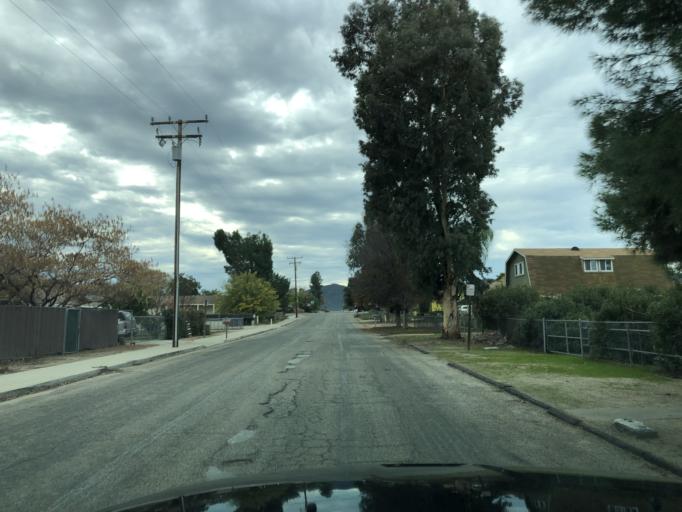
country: US
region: California
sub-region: Riverside County
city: Wildomar
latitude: 33.6209
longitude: -117.2798
